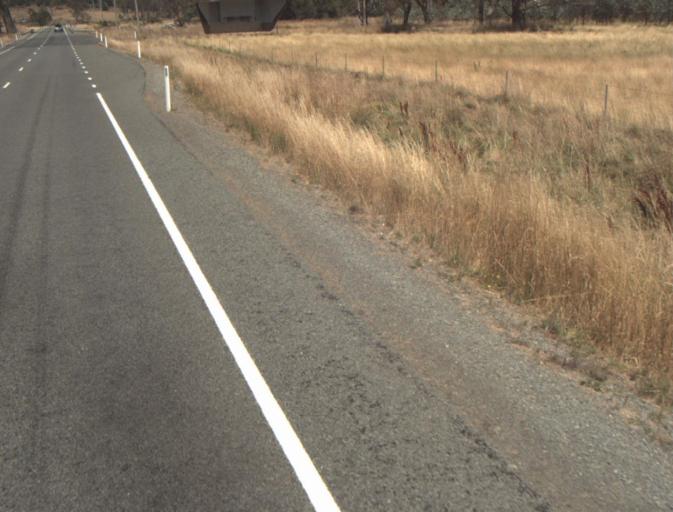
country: AU
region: Tasmania
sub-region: Launceston
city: Newstead
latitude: -41.3558
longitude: 147.3385
